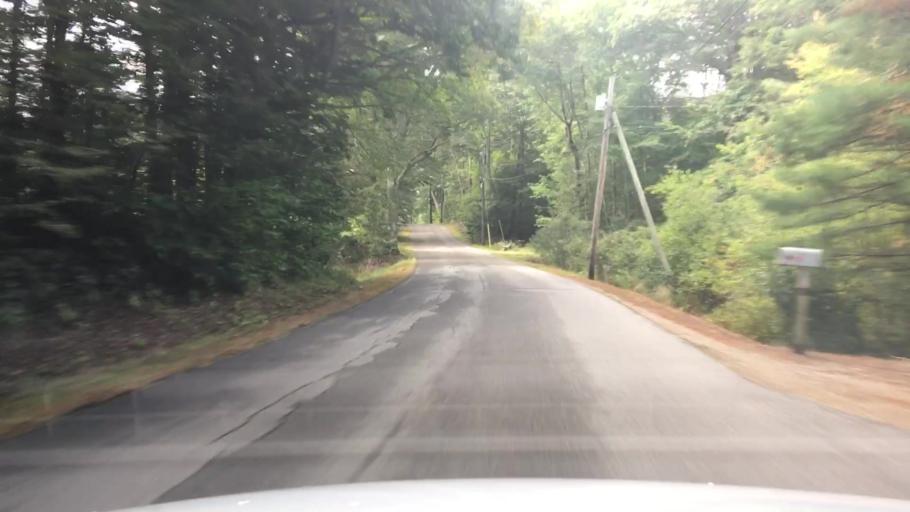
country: US
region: Maine
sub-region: York County
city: Kittery Point
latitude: 43.1158
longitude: -70.6830
